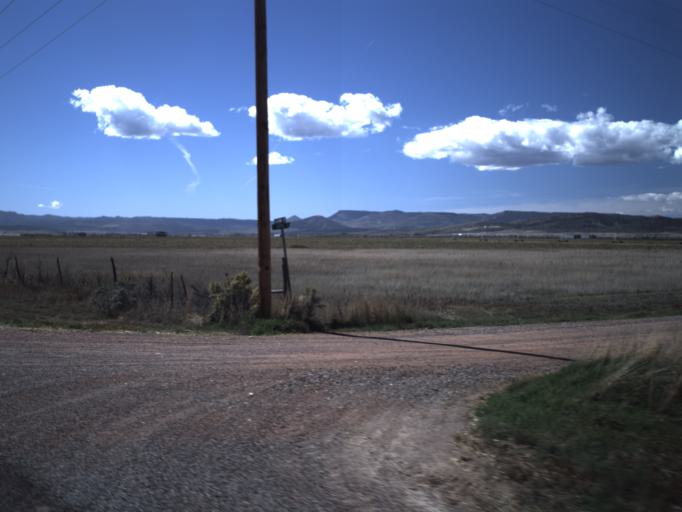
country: US
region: Utah
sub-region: Washington County
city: Enterprise
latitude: 37.6486
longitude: -113.6612
